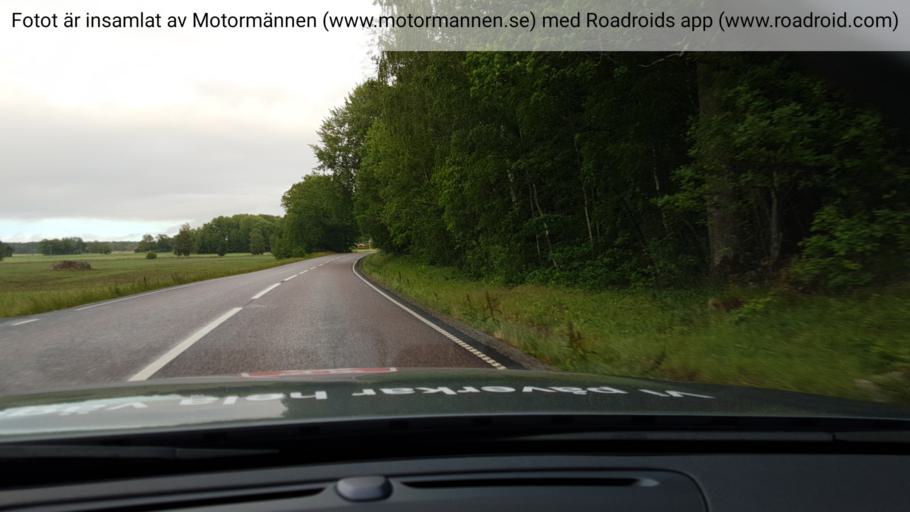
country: SE
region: Soedermanland
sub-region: Eskilstuna Kommun
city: Kvicksund
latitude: 59.3174
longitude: 16.2869
